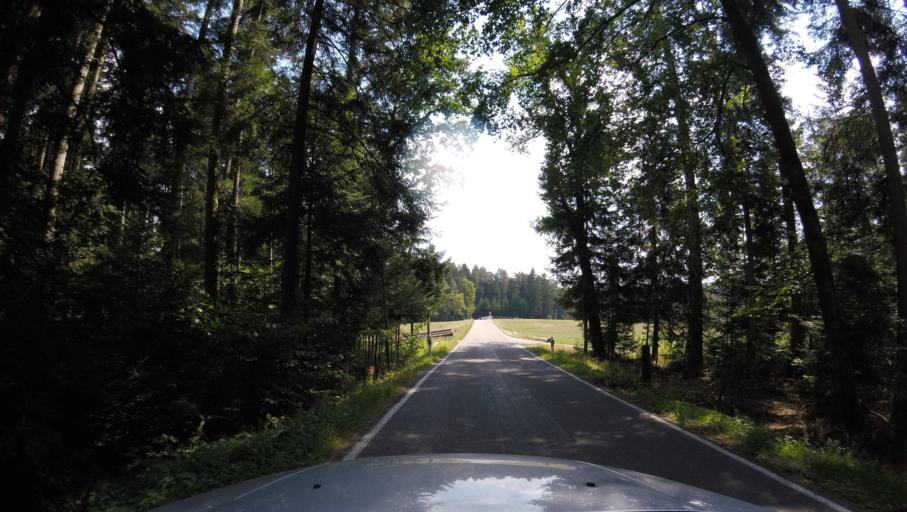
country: DE
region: Baden-Wuerttemberg
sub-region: Regierungsbezirk Stuttgart
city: Alfdorf
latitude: 48.8650
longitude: 9.7103
